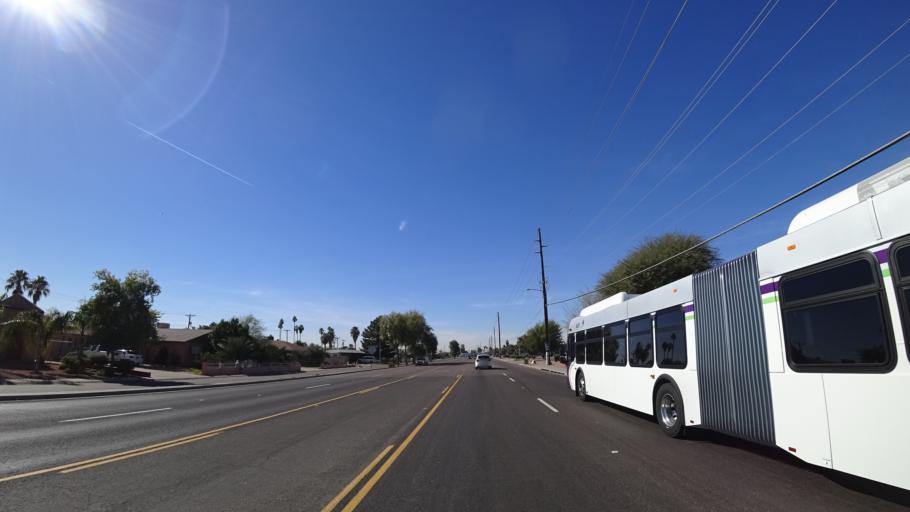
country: US
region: Arizona
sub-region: Maricopa County
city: Glendale
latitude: 33.5096
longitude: -112.1820
